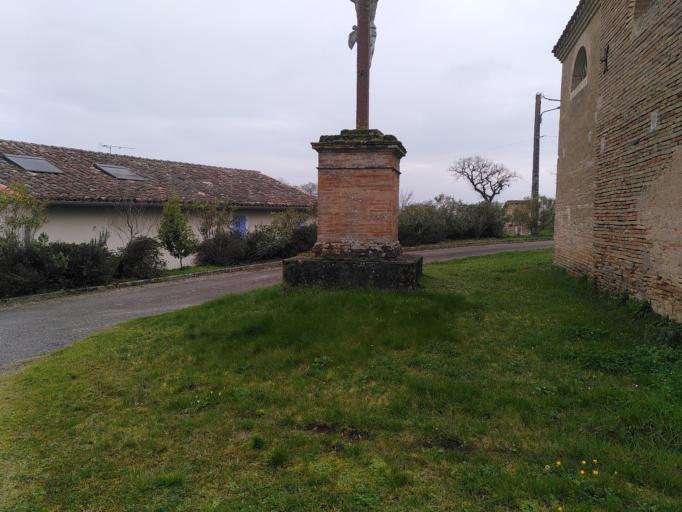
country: FR
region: Midi-Pyrenees
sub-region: Departement du Tarn-et-Garonne
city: Beaumont-de-Lomagne
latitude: 43.7869
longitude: 0.9979
